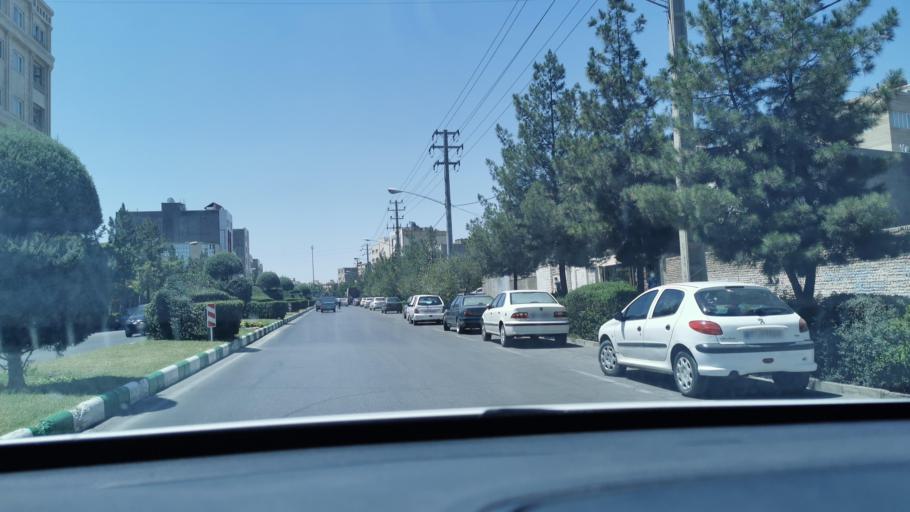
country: IR
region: Razavi Khorasan
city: Mashhad
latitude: 36.3387
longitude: 59.4860
